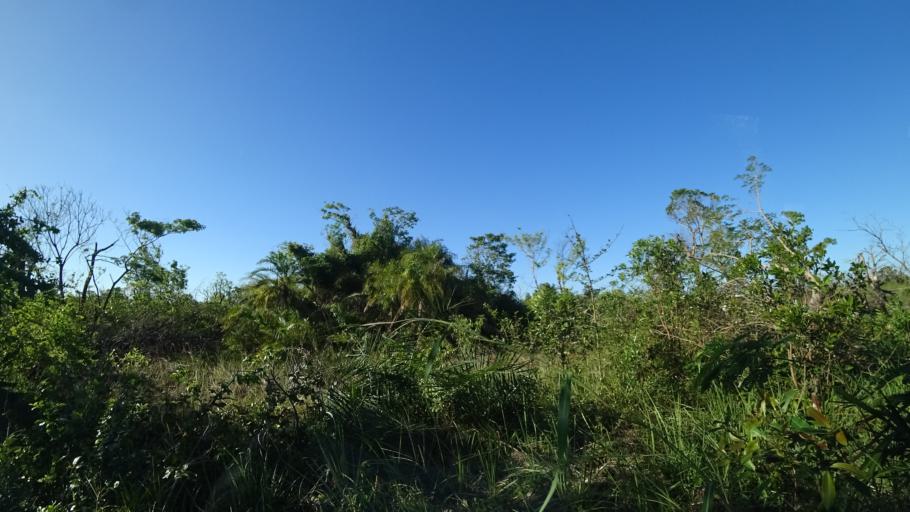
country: MZ
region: Sofala
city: Beira
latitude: -19.5712
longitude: 35.2480
